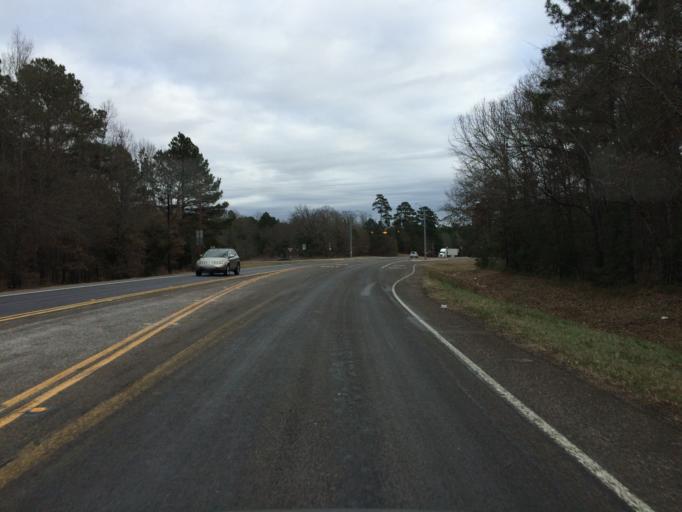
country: US
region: Texas
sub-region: Wood County
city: Mineola
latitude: 32.6880
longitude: -95.4716
